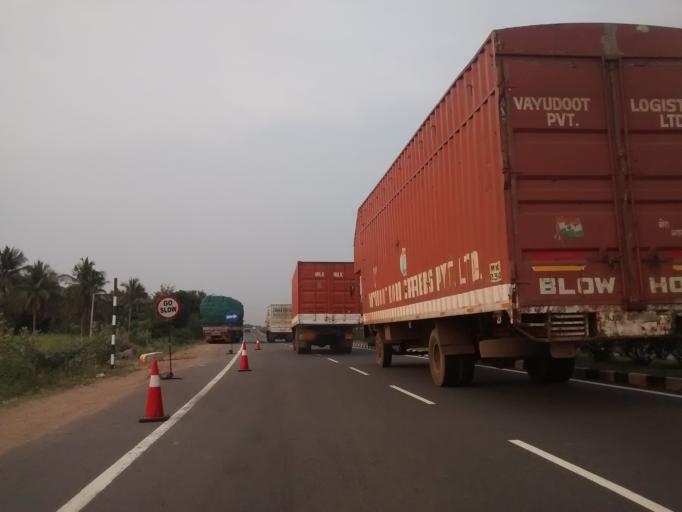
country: IN
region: Tamil Nadu
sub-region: Dharmapuri
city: Dharmapuri
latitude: 12.2202
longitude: 78.1915
